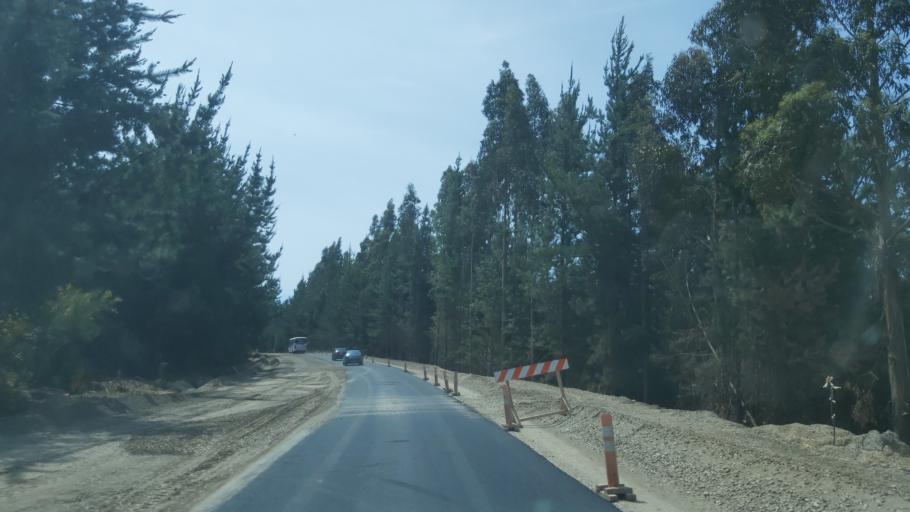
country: CL
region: Maule
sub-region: Provincia de Talca
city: Constitucion
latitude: -35.3800
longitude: -72.4211
